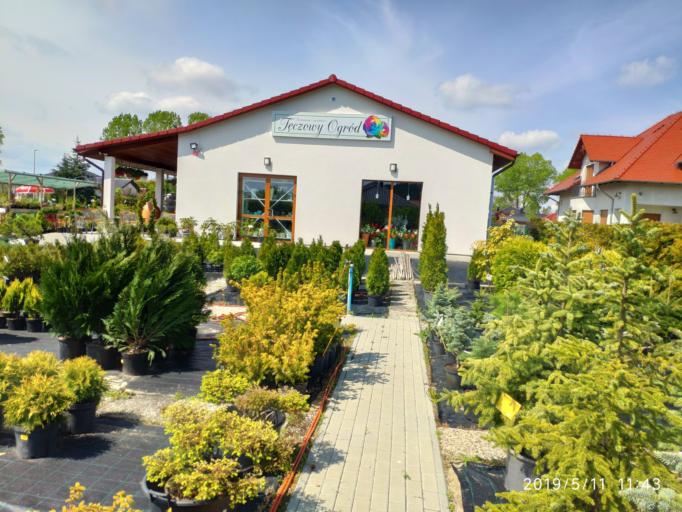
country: PL
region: Lubusz
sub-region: Zielona Gora
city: Zielona Gora
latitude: 51.9735
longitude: 15.5350
